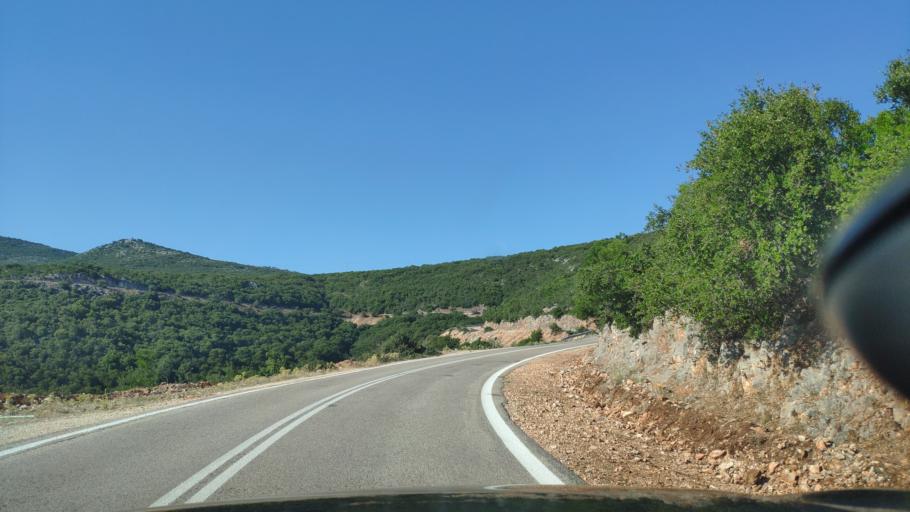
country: GR
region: West Greece
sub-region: Nomos Aitolias kai Akarnanias
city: Archontochorion
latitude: 38.6981
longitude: 21.0805
